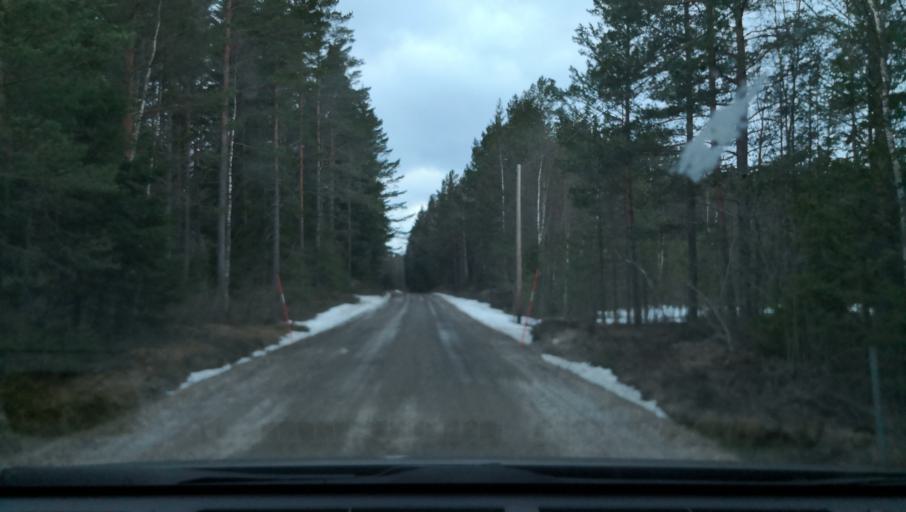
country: SE
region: Vaestmanland
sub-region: Kopings Kommun
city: Kolsva
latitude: 59.6010
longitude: 15.6632
